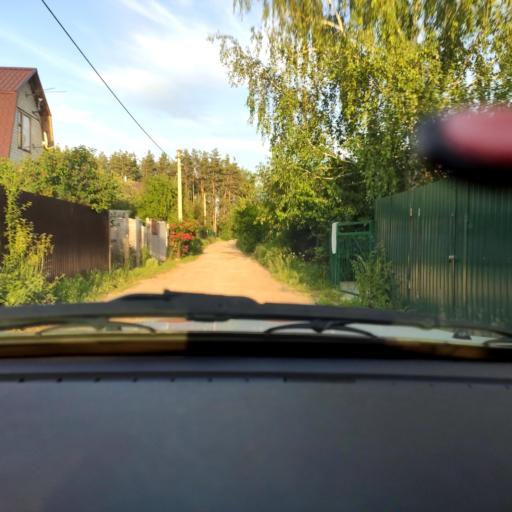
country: RU
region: Voronezj
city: Podgornoye
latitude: 51.8340
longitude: 39.1936
